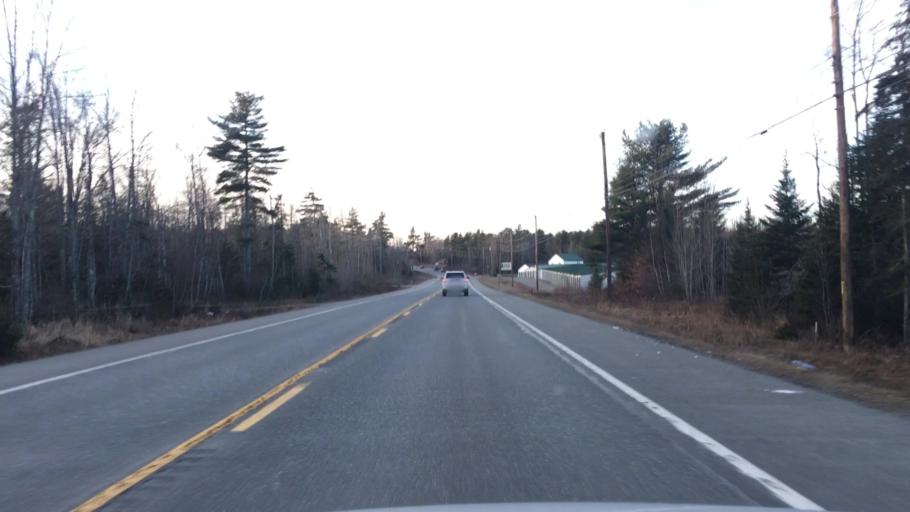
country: US
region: Maine
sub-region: Hancock County
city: Ellsworth
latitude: 44.5731
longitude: -68.4640
